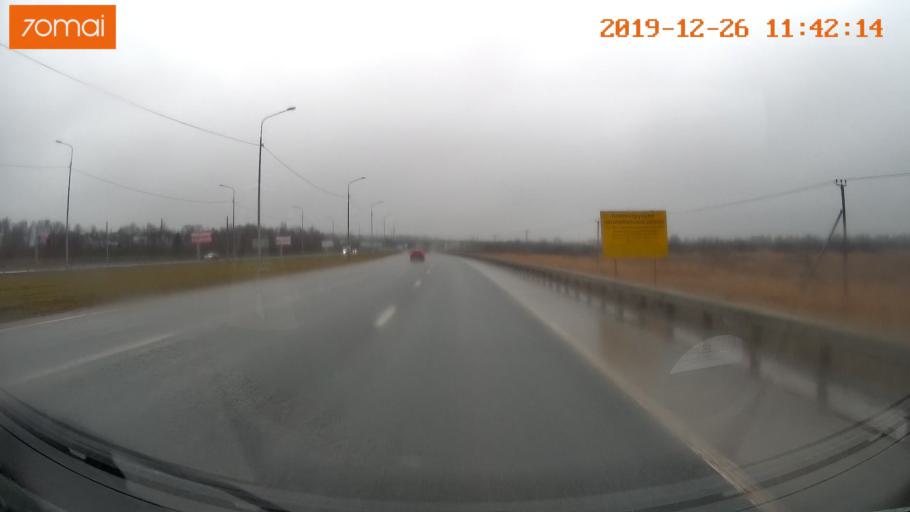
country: RU
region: Vologda
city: Sheksna
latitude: 59.2120
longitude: 38.5274
